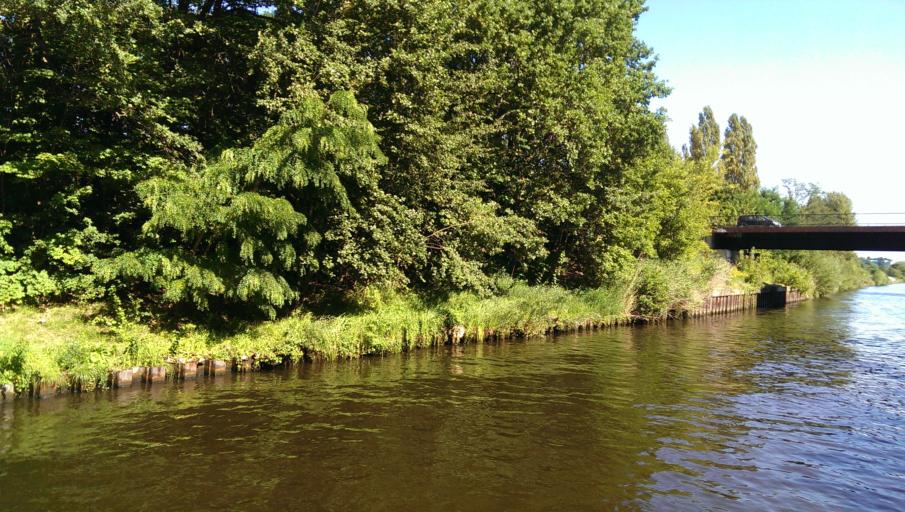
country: DE
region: Brandenburg
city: Kleinmachnow
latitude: 52.4010
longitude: 13.2387
